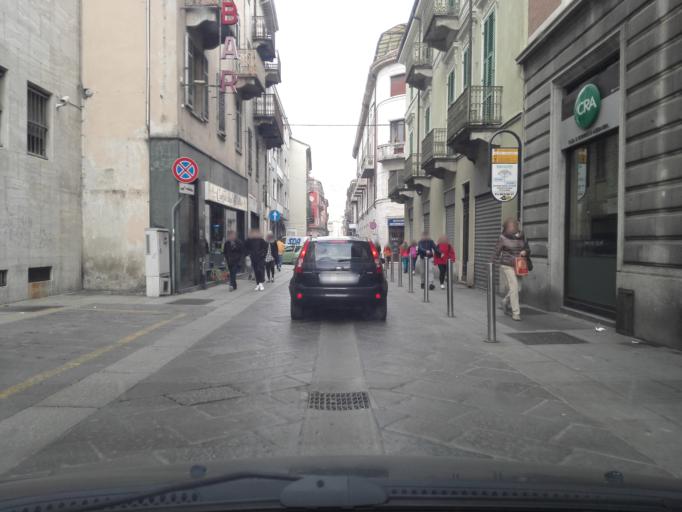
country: IT
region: Piedmont
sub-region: Provincia di Alessandria
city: Alessandria
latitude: 44.9139
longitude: 8.6168
